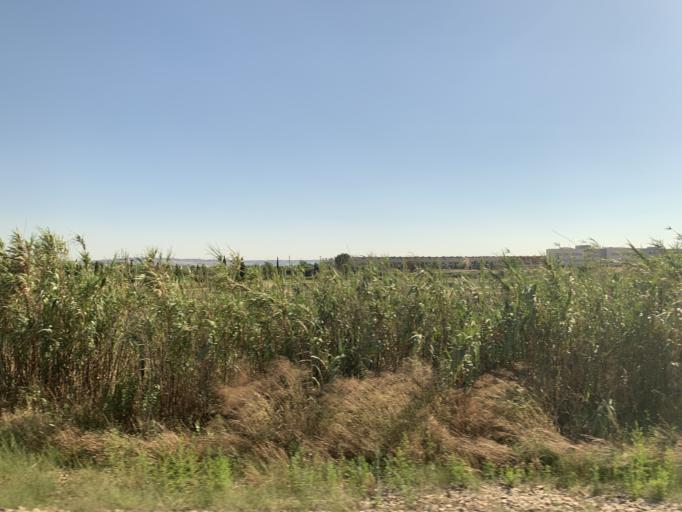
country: ES
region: Aragon
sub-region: Provincia de Zaragoza
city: Utebo
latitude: 41.7055
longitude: -0.9896
